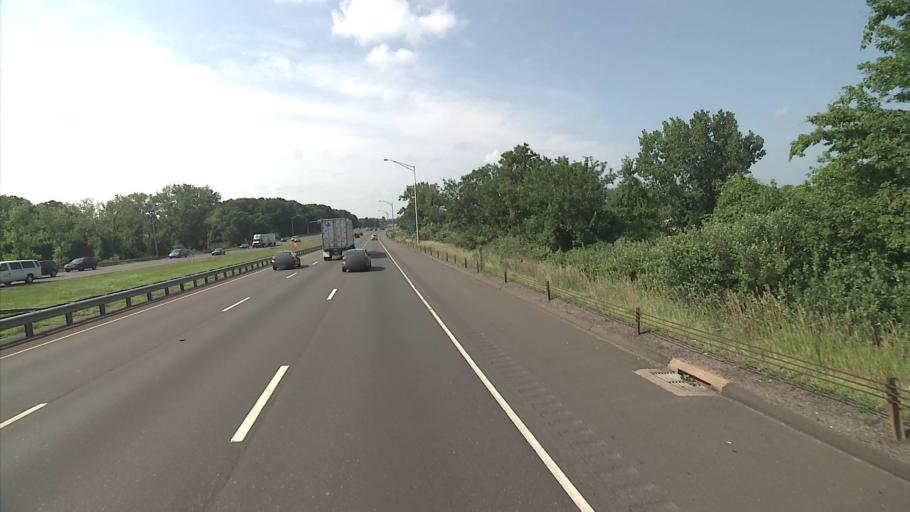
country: US
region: Connecticut
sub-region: New Haven County
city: North Haven
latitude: 41.3853
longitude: -72.8664
